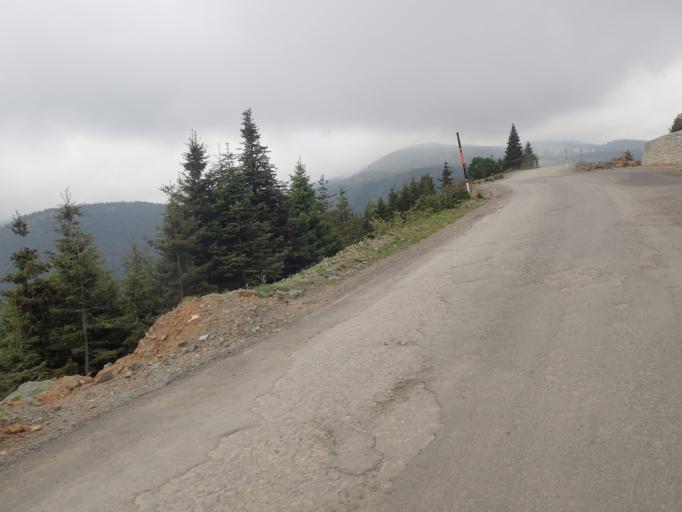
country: TR
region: Ordu
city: Topcam
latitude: 40.6605
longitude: 37.9408
